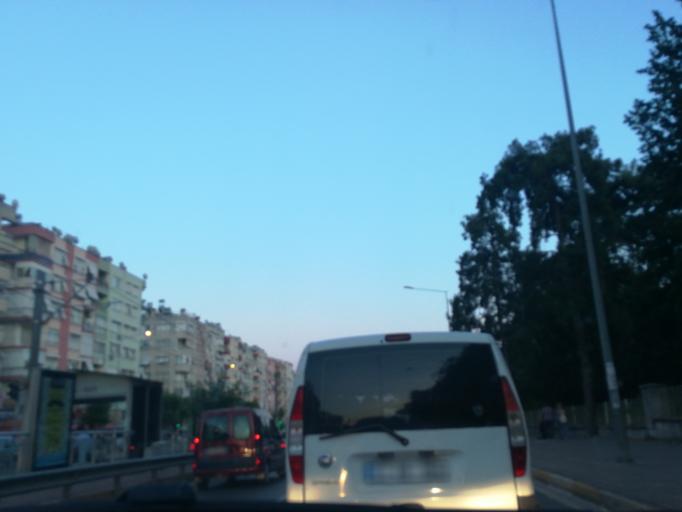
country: TR
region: Antalya
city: Antalya
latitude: 36.9139
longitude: 30.6763
